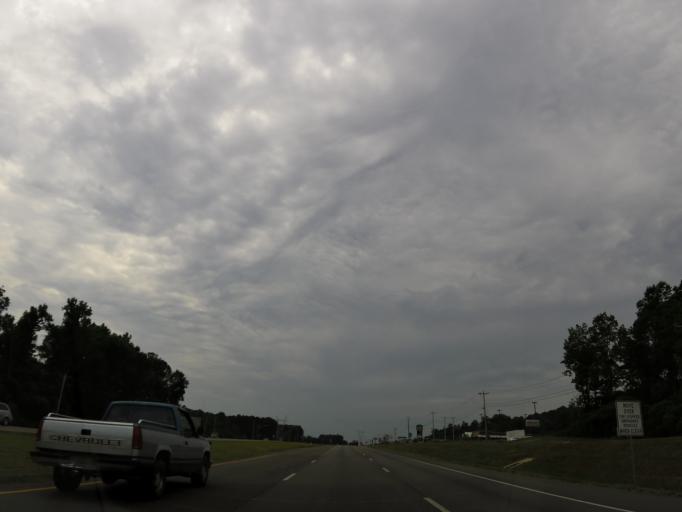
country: US
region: Alabama
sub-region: Jackson County
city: Scottsboro
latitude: 34.6589
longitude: -86.0194
